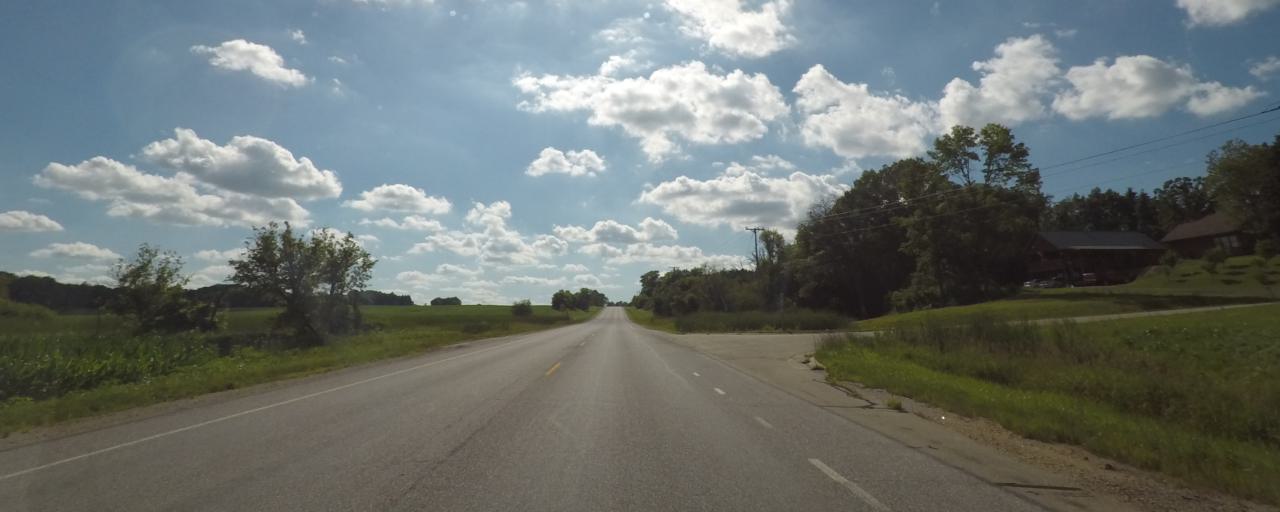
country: US
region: Wisconsin
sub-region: Dane County
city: Stoughton
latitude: 42.9198
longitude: -89.1209
